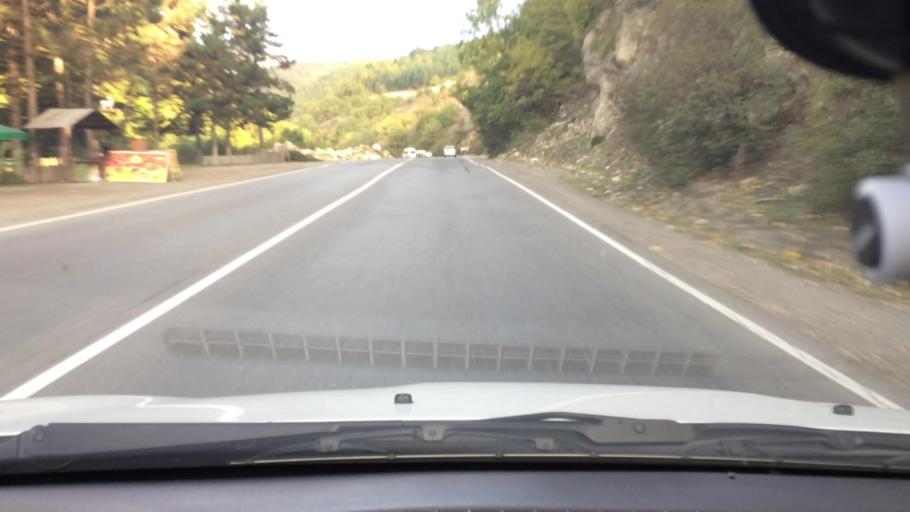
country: GE
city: Surami
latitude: 42.0364
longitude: 43.5194
